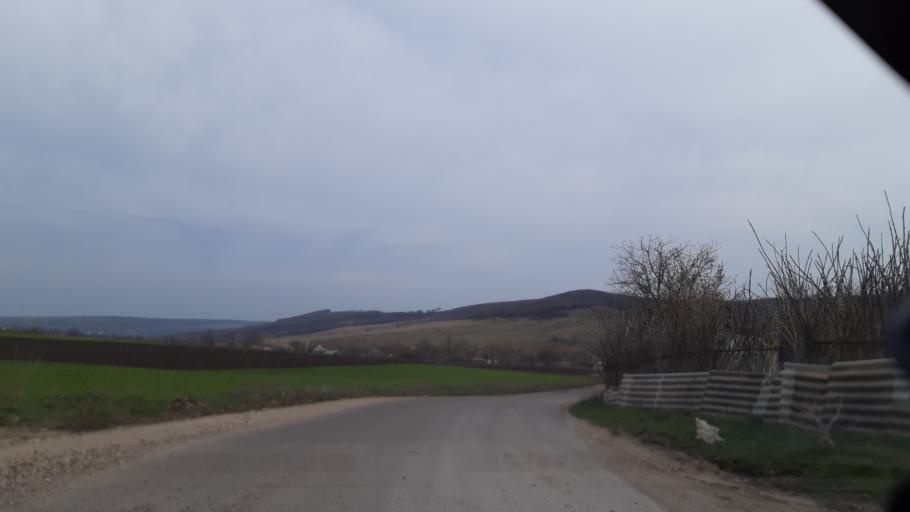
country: MD
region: Soldanesti
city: Soldanesti
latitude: 47.6886
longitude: 28.7444
